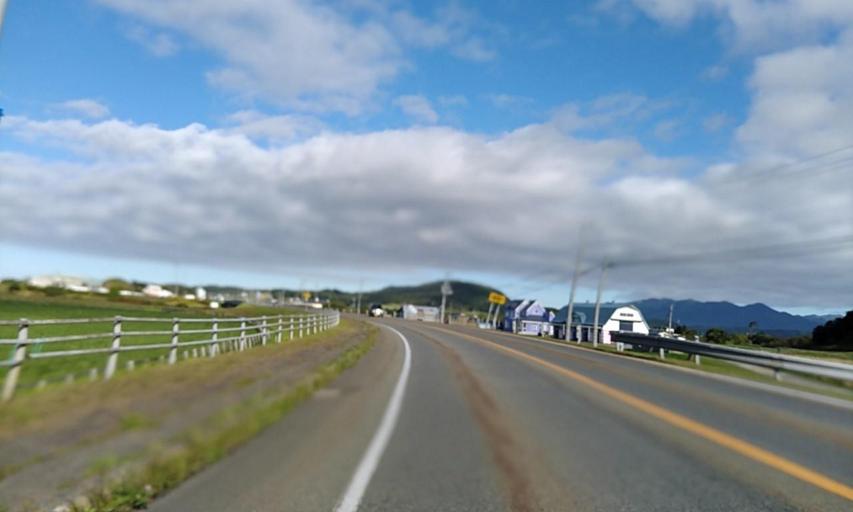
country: JP
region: Hokkaido
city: Shizunai-furukawacho
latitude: 42.2182
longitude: 142.6407
